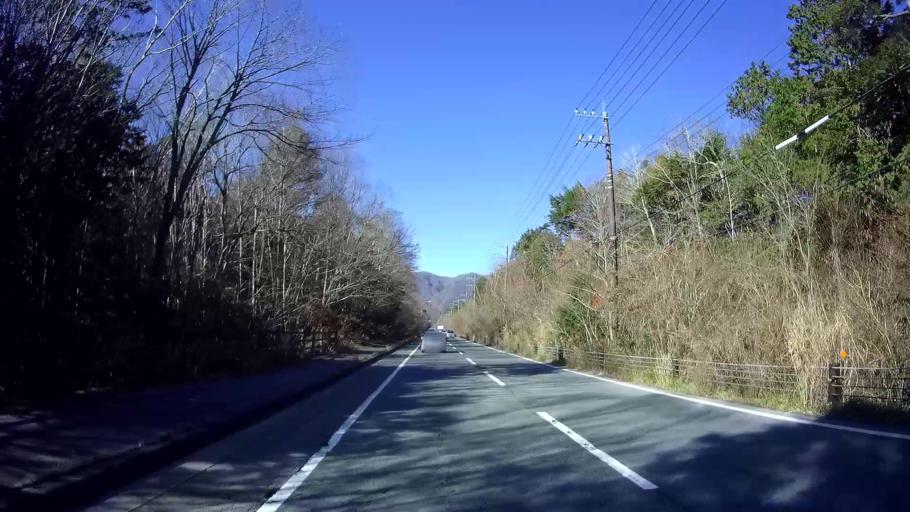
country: JP
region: Yamanashi
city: Fujikawaguchiko
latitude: 35.4834
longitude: 138.6520
